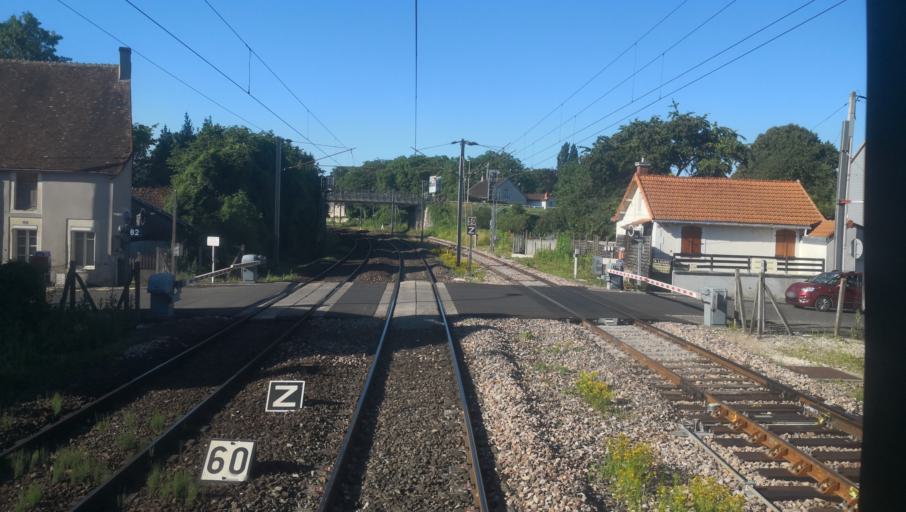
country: FR
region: Bourgogne
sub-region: Departement de la Nievre
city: Cosne-Cours-sur-Loire
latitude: 47.4115
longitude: 2.9320
